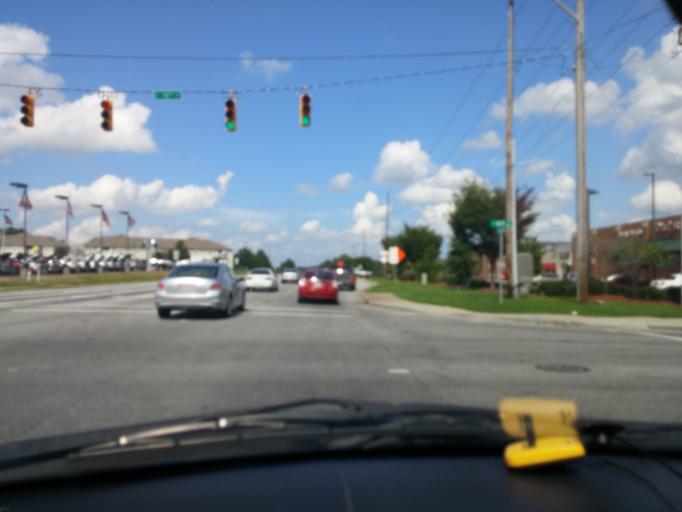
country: US
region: North Carolina
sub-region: Pitt County
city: Greenville
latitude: 35.6004
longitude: -77.3350
